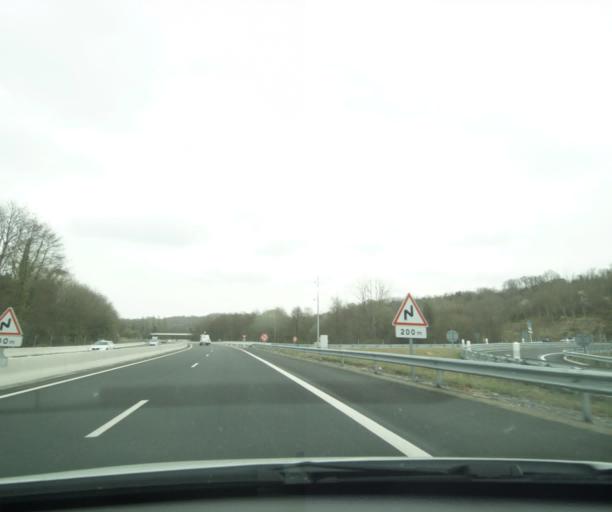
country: FR
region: Aquitaine
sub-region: Departement des Pyrenees-Atlantiques
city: Mouguerre
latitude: 43.4646
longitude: -1.4285
